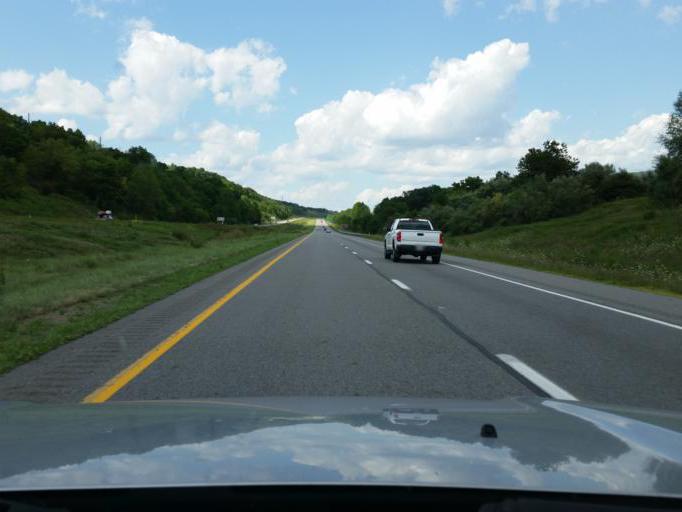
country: US
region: Pennsylvania
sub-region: Bedford County
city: Bedford
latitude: 40.1180
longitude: -78.5203
